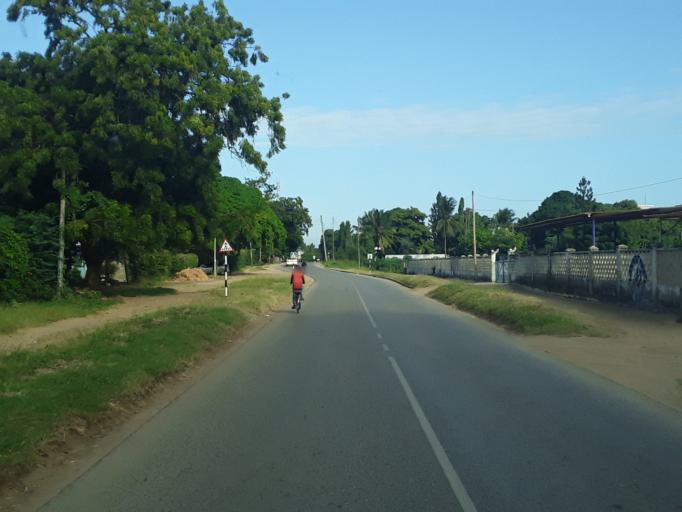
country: TZ
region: Tanga
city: Tanga
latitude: -5.0728
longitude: 39.1094
